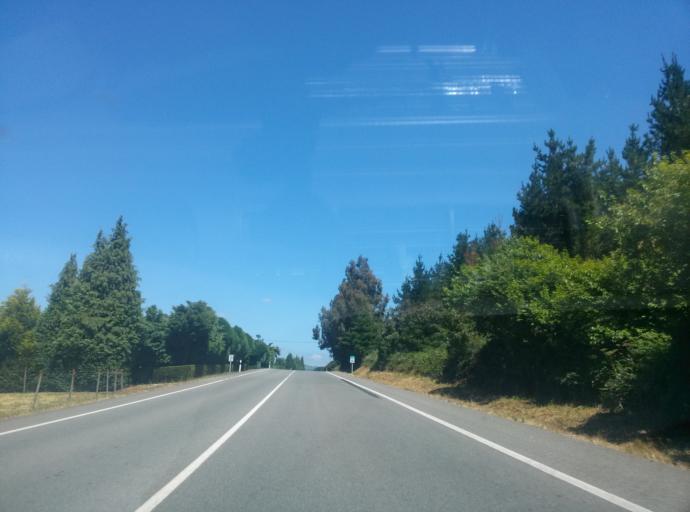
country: ES
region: Galicia
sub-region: Provincia de Lugo
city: Castro de Rei
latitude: 43.2319
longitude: -7.3625
